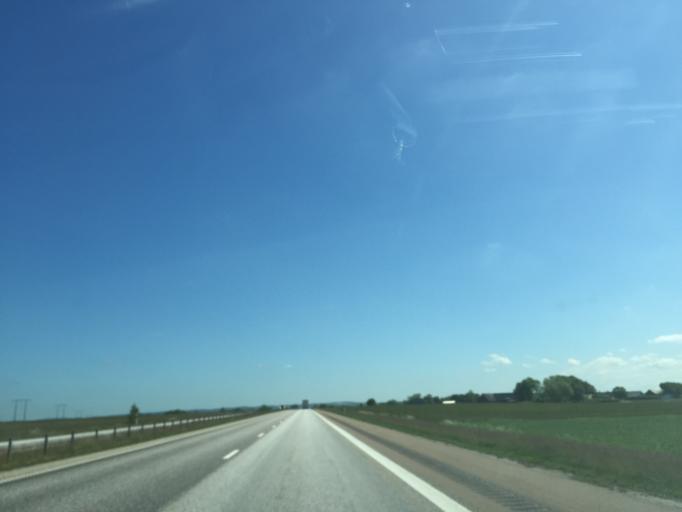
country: SE
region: Skane
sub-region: Astorps Kommun
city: Astorp
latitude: 56.1635
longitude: 12.9706
